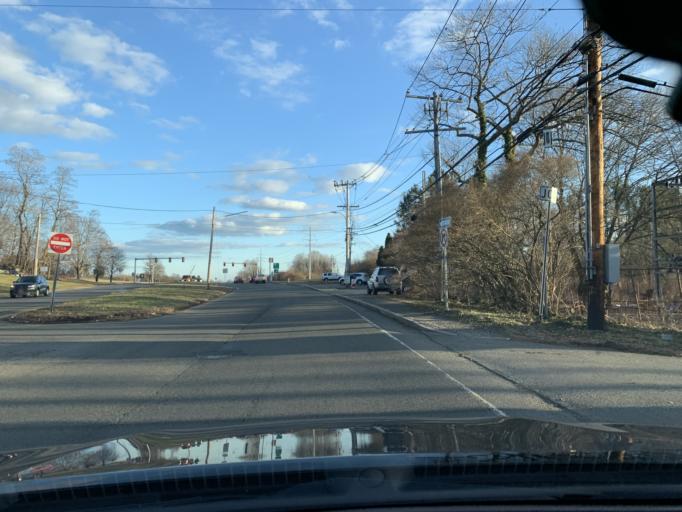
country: US
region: Massachusetts
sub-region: Essex County
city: Danvers
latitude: 42.5867
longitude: -70.9721
